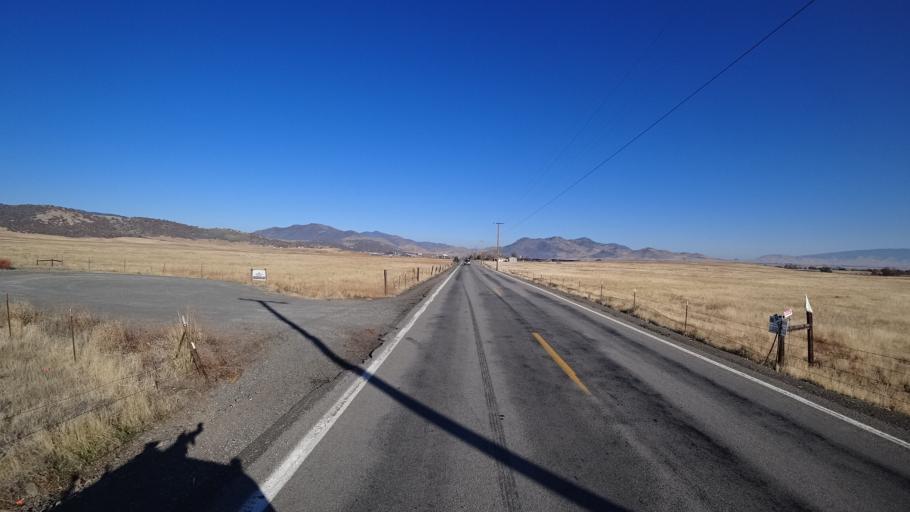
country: US
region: California
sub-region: Siskiyou County
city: Yreka
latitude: 41.7166
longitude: -122.5935
